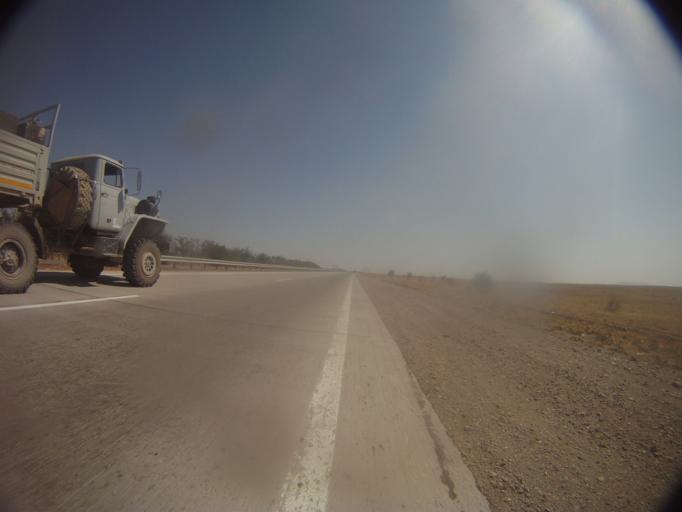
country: KZ
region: Zhambyl
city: Taraz
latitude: 42.7933
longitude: 71.0754
